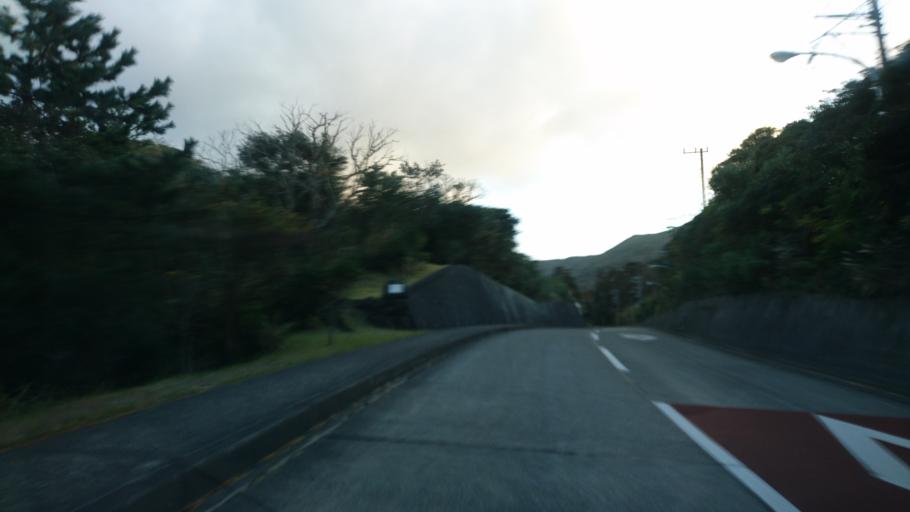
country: JP
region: Shizuoka
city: Shimoda
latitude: 34.3674
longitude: 139.2587
